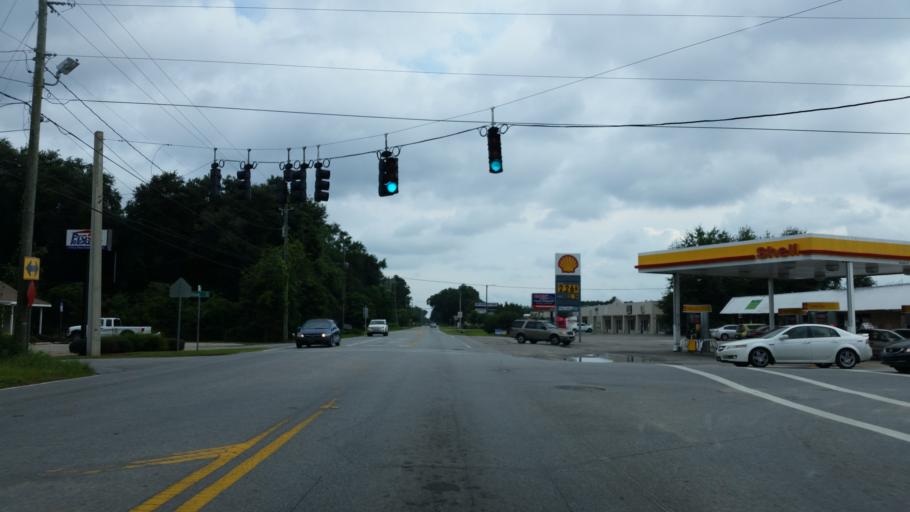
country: US
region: Florida
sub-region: Santa Rosa County
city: Pace
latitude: 30.6150
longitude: -87.1487
